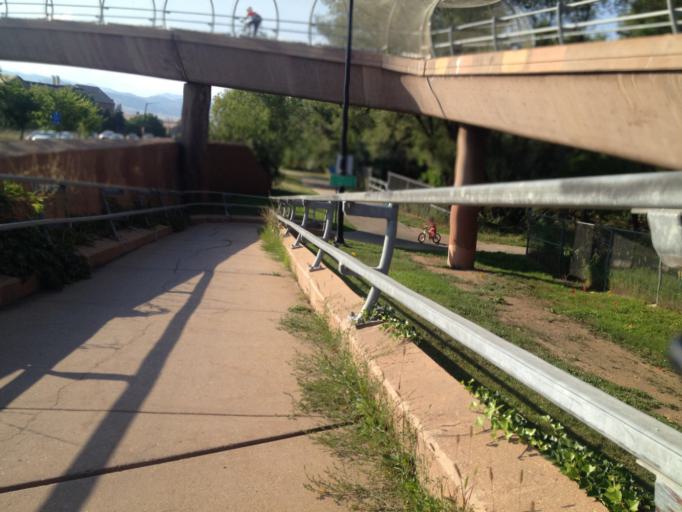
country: US
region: Colorado
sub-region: Boulder County
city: Boulder
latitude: 40.0068
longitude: -105.2380
